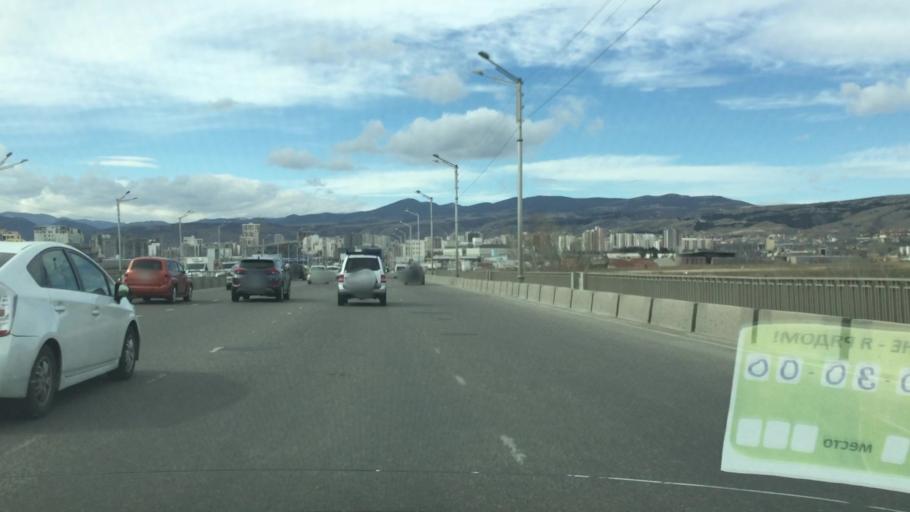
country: GE
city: Zahesi
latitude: 41.7861
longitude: 44.7874
